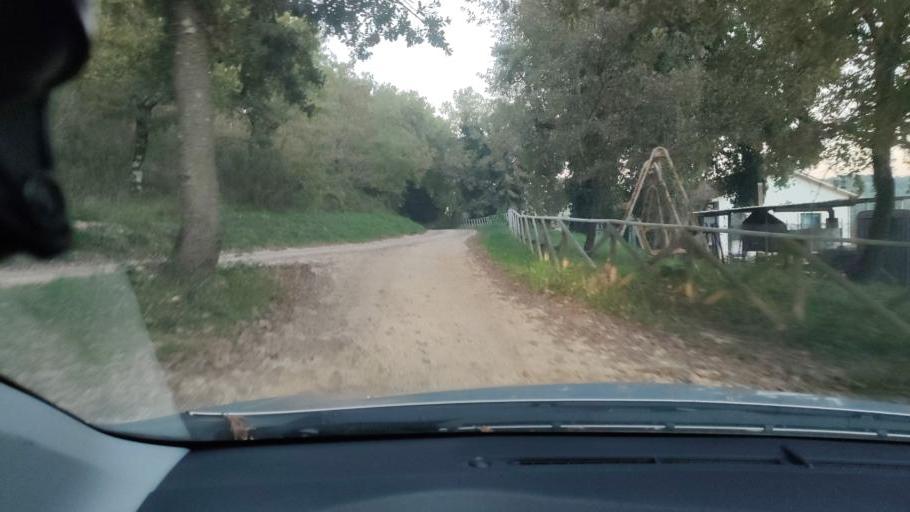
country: IT
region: Umbria
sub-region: Provincia di Terni
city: Amelia
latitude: 42.5969
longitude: 12.4333
